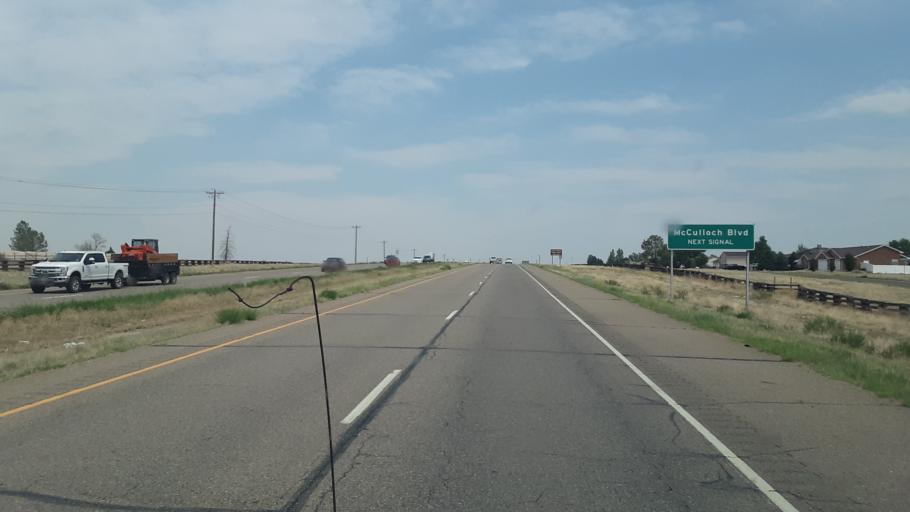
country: US
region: Colorado
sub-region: Pueblo County
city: Pueblo West
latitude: 38.3385
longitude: -104.7548
